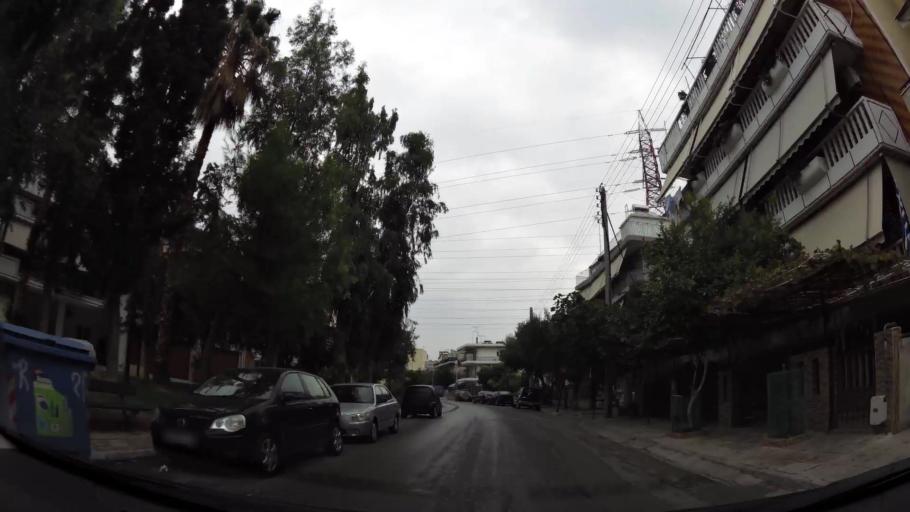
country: GR
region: Attica
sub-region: Nomarchia Athinas
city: Agia Varvara
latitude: 37.9854
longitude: 23.6667
